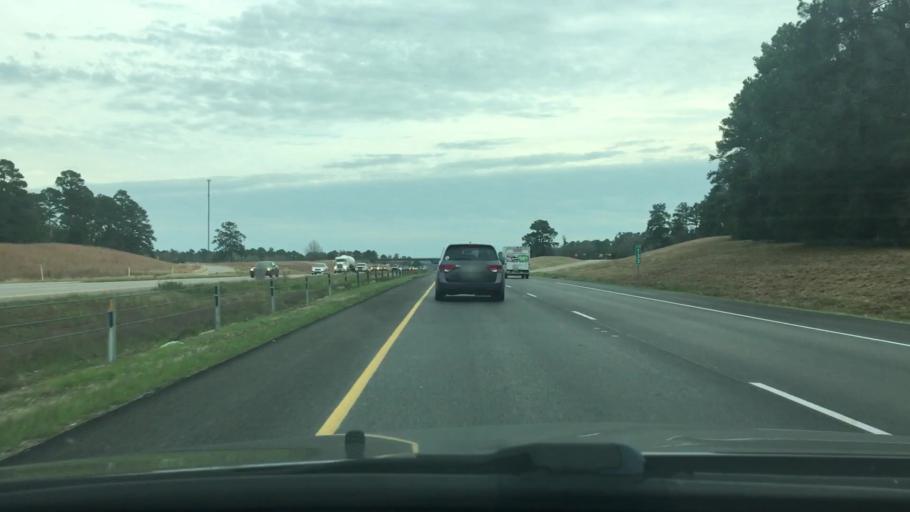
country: US
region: Texas
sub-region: Madison County
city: Madisonville
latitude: 30.8771
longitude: -95.7634
